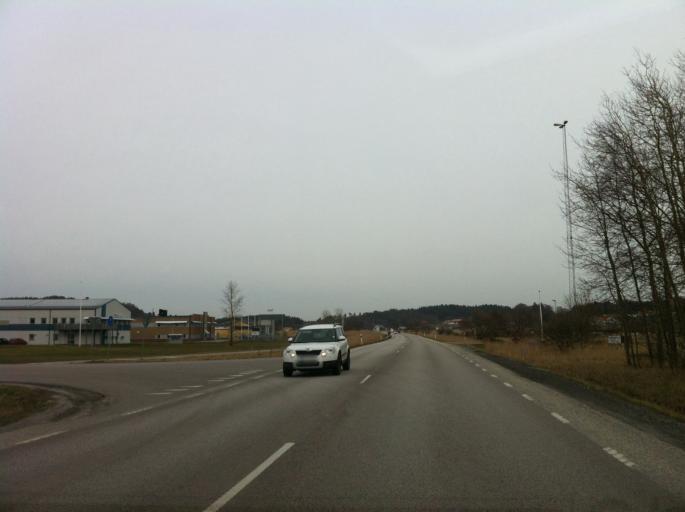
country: SE
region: Vaestra Goetaland
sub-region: Tjorns Kommun
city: Myggenas
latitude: 58.0228
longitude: 11.6942
